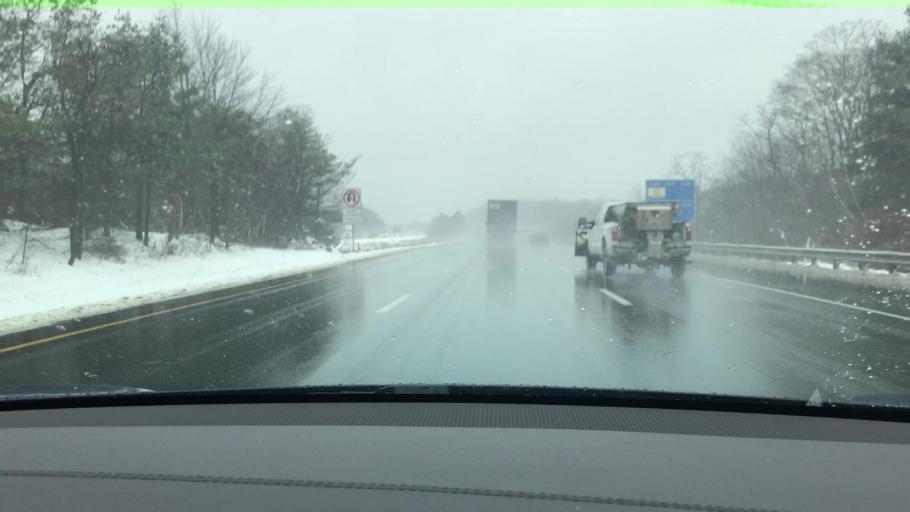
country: US
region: Massachusetts
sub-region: Worcester County
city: Shrewsbury
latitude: 42.3243
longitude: -71.7110
